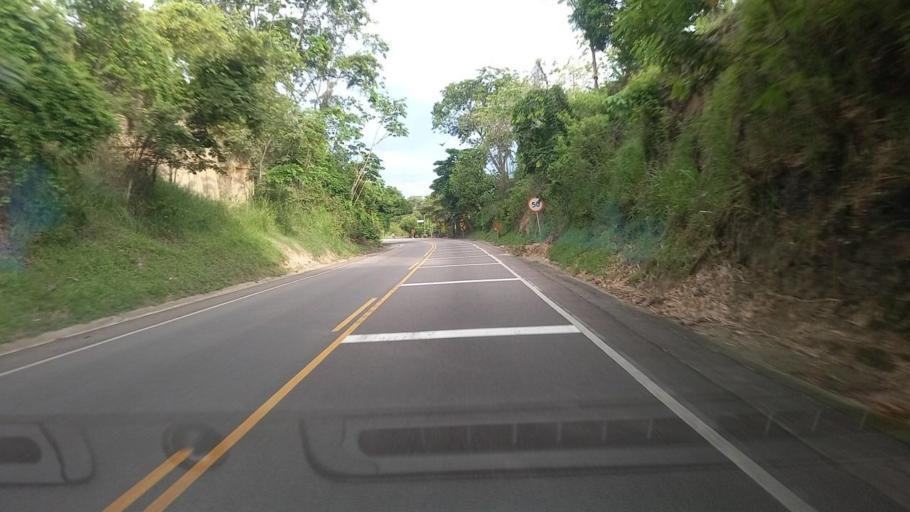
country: CO
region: Santander
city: Puerto Parra
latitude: 6.4859
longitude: -74.1828
